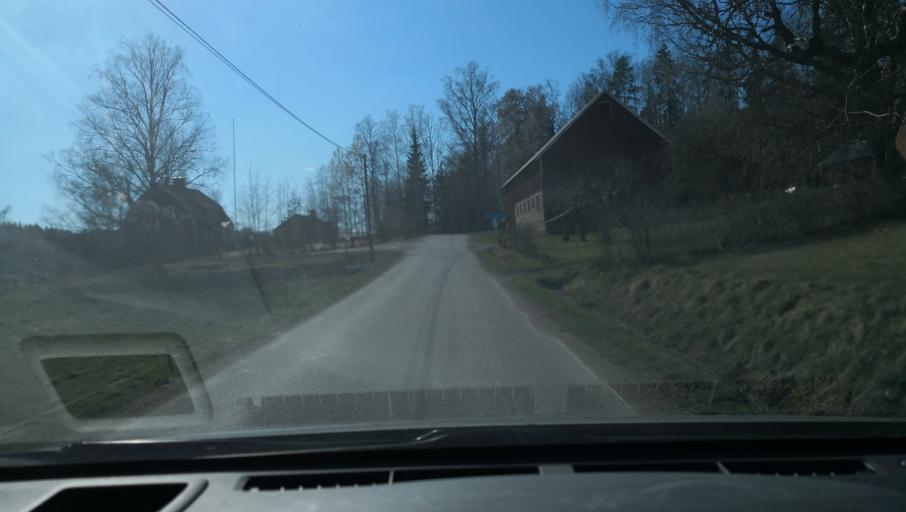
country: SE
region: Vaestmanland
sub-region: Sala Kommun
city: Sala
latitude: 60.0768
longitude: 16.4822
